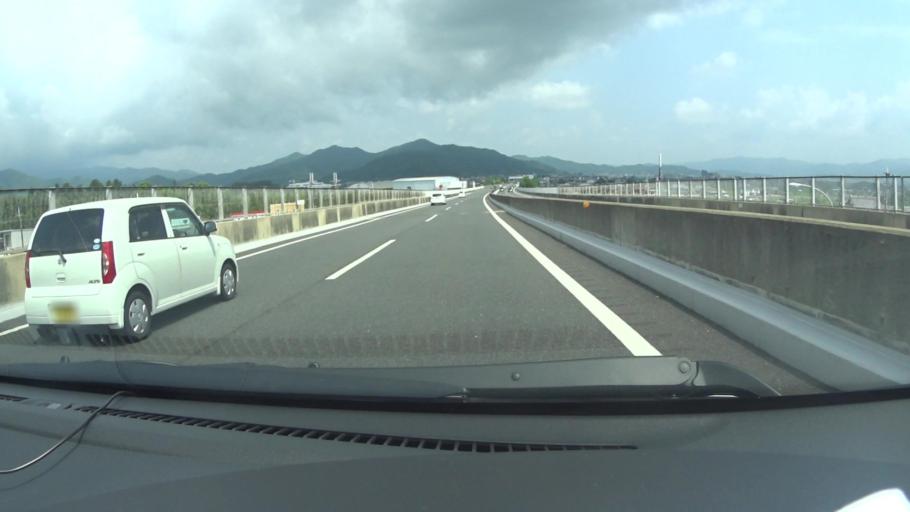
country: JP
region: Kyoto
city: Kameoka
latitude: 35.0080
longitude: 135.5620
